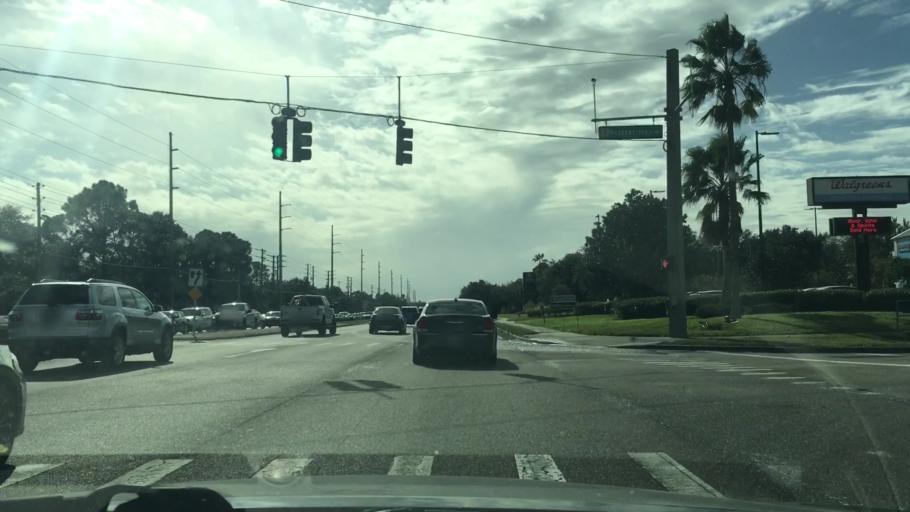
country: US
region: Florida
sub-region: Osceola County
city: Celebration
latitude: 28.3707
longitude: -81.5035
